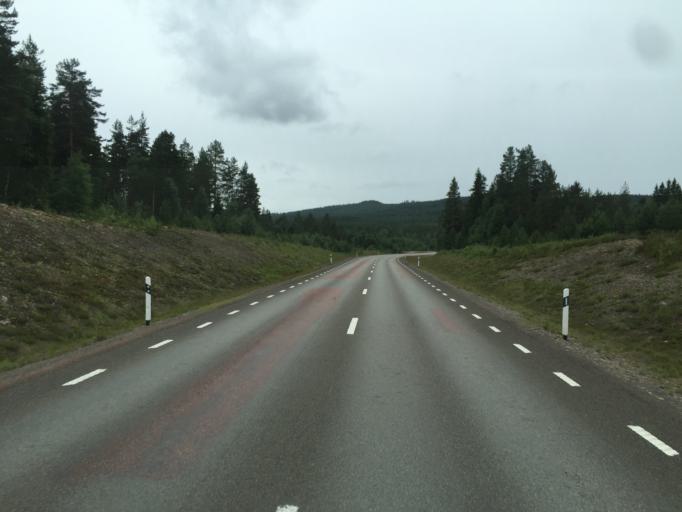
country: SE
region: Dalarna
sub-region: Malung-Saelens kommun
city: Malung
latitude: 60.6064
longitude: 13.5874
